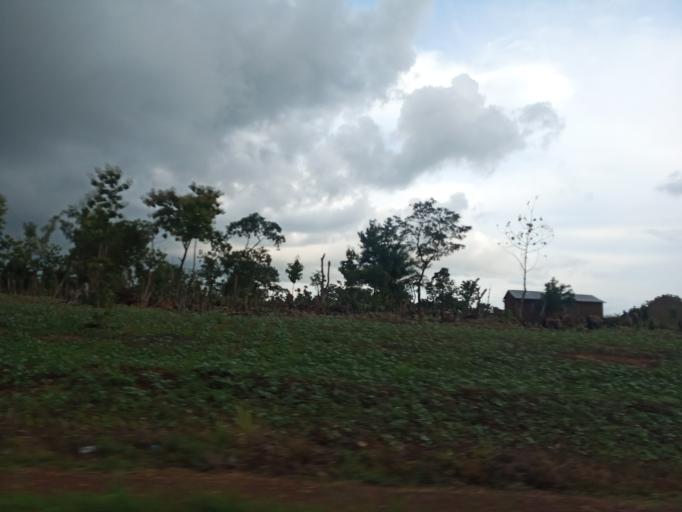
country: TG
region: Centrale
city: Sotouboua
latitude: 8.5946
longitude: 0.9965
